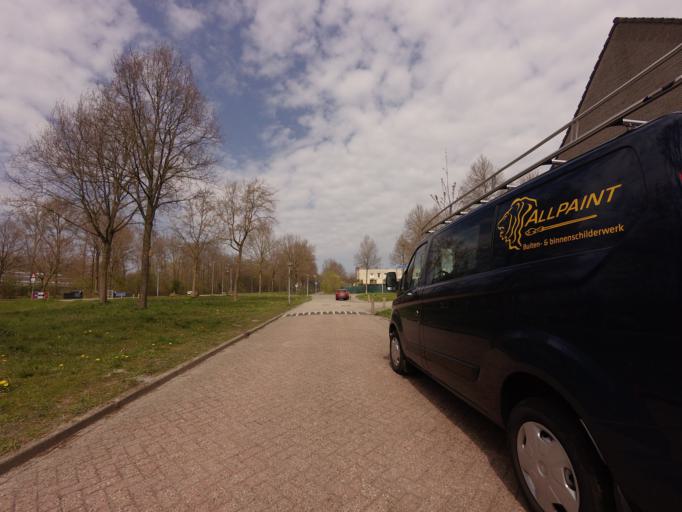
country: NL
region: Flevoland
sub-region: Gemeente Zeewolde
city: Zeewolde
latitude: 52.3218
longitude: 5.5317
